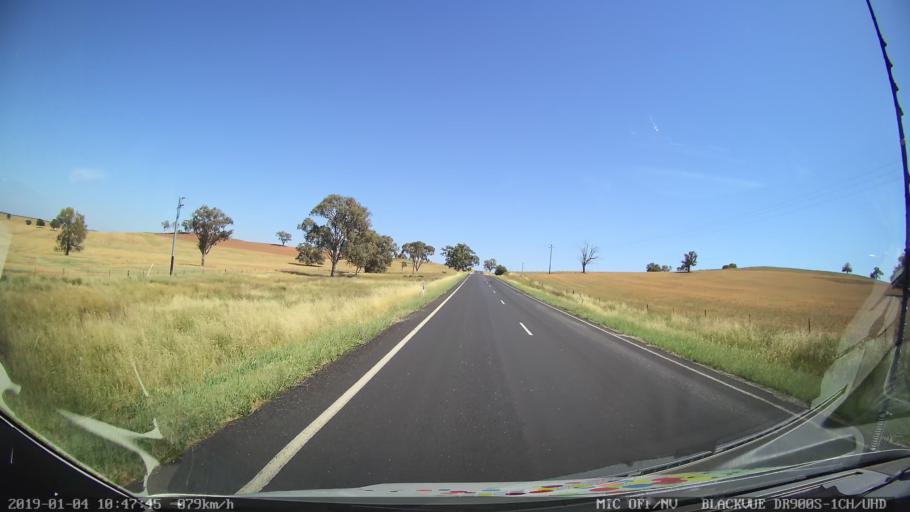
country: AU
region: New South Wales
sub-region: Cabonne
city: Molong
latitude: -33.2668
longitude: 148.7176
